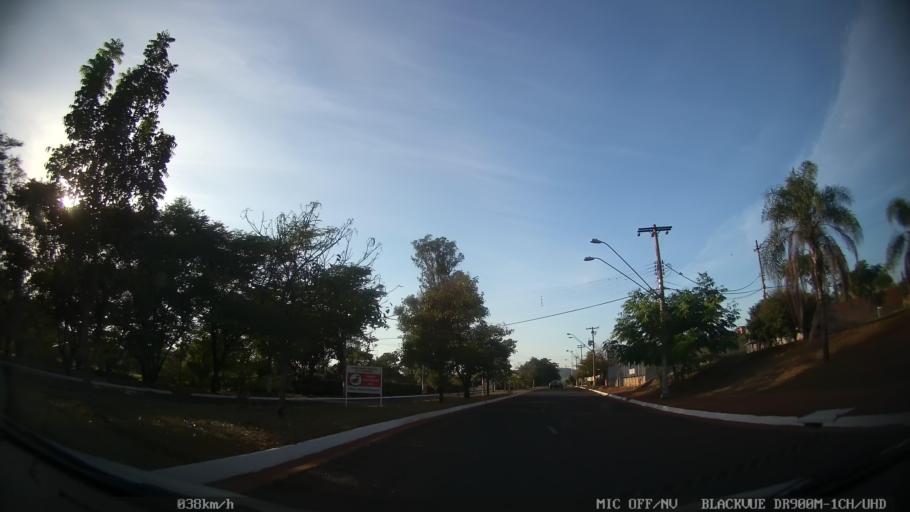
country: BR
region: Sao Paulo
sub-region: Ribeirao Preto
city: Ribeirao Preto
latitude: -21.2161
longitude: -47.7807
